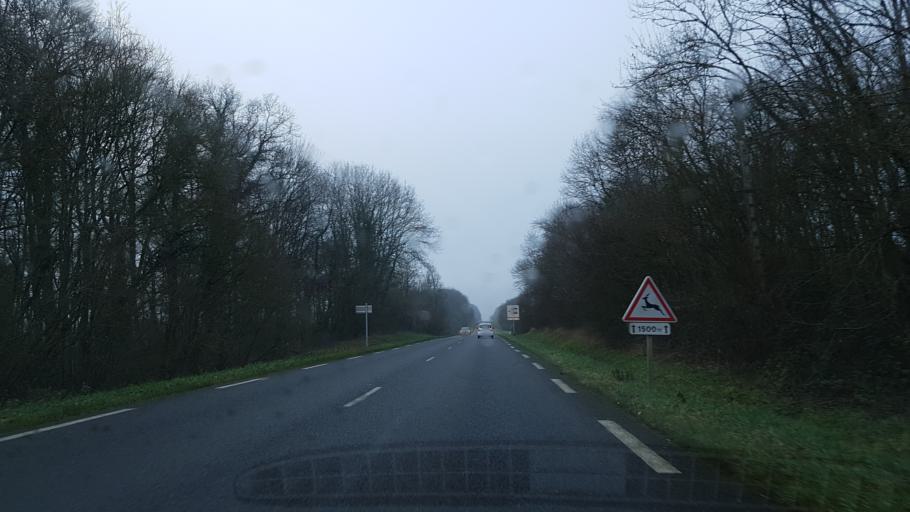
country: FR
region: Lorraine
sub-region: Departement de la Moselle
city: Bliesbruck
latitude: 49.0942
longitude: 7.1894
